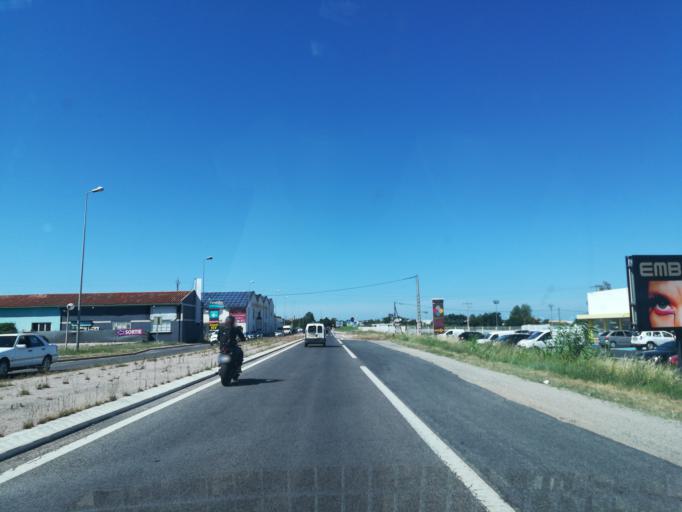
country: FR
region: Languedoc-Roussillon
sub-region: Departement des Pyrenees-Orientales
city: Pollestres
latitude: 42.6377
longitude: 2.8743
